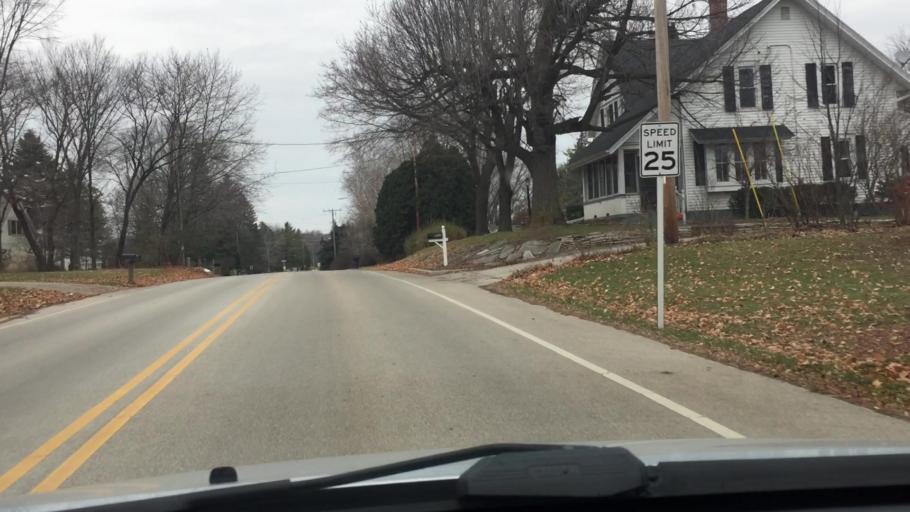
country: US
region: Wisconsin
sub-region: Ozaukee County
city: Thiensville
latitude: 43.2404
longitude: -87.9812
